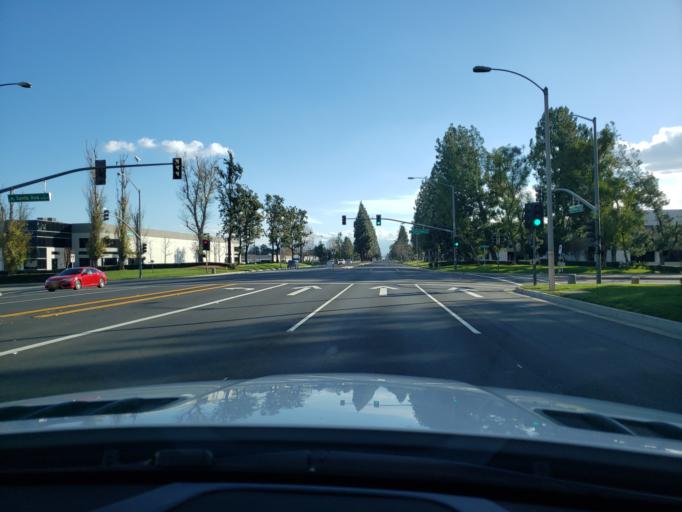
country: US
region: California
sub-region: San Bernardino County
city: Rancho Cucamonga
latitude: 34.0559
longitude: -117.5583
